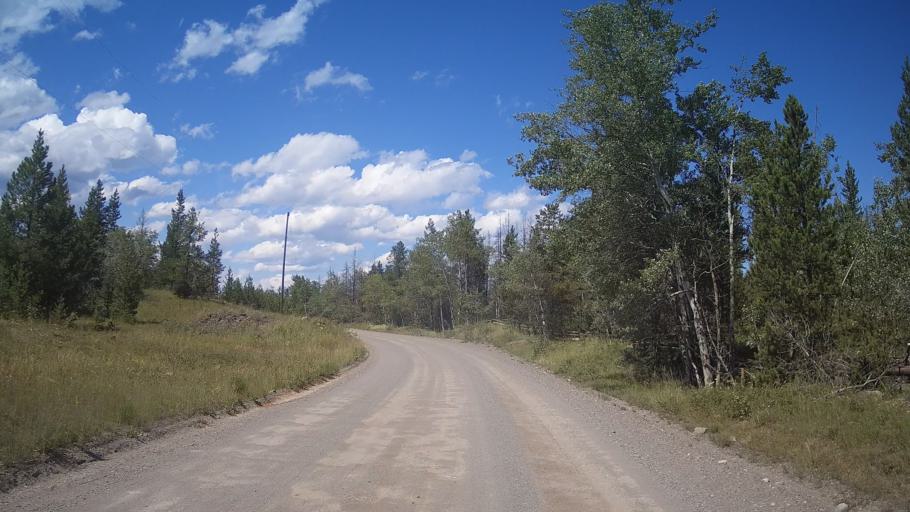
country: CA
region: British Columbia
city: Cache Creek
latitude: 51.2492
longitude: -121.6641
